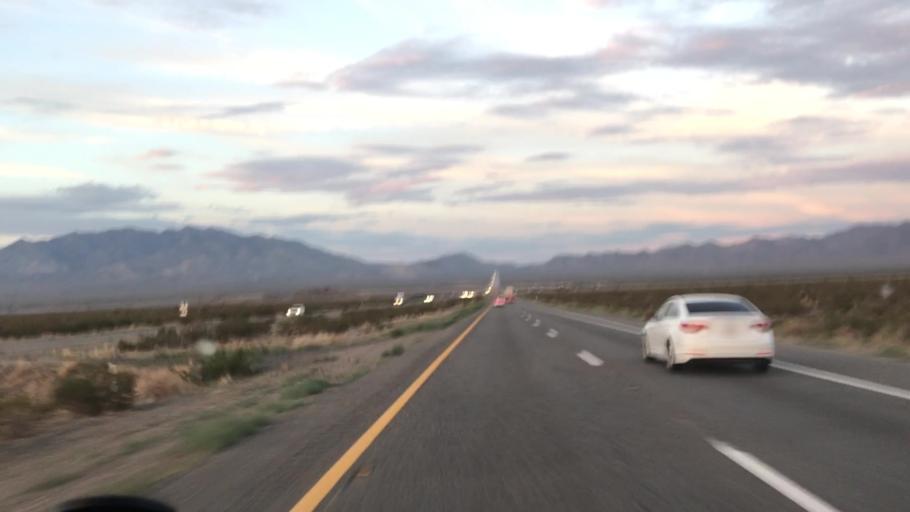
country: US
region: Nevada
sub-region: Clark County
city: Sandy Valley
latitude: 35.4282
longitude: -115.7187
